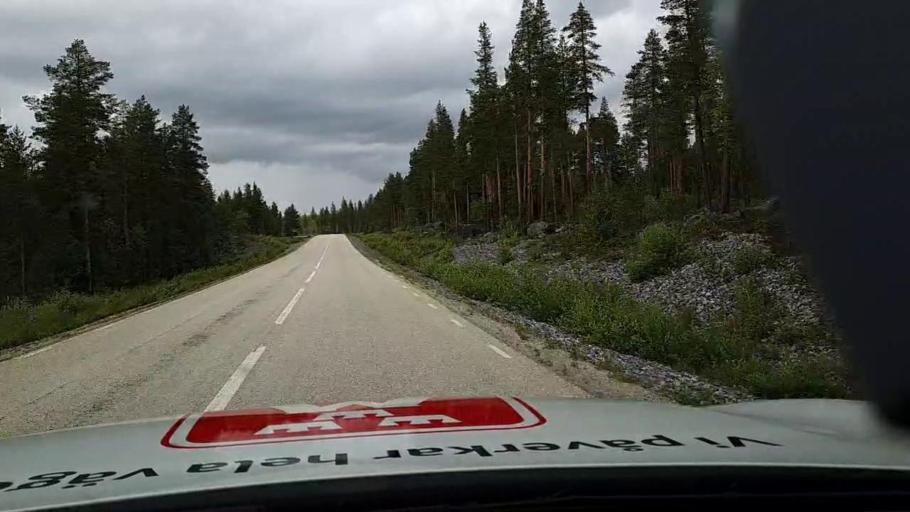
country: SE
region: Jaemtland
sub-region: Are Kommun
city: Jarpen
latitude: 62.8400
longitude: 13.4121
